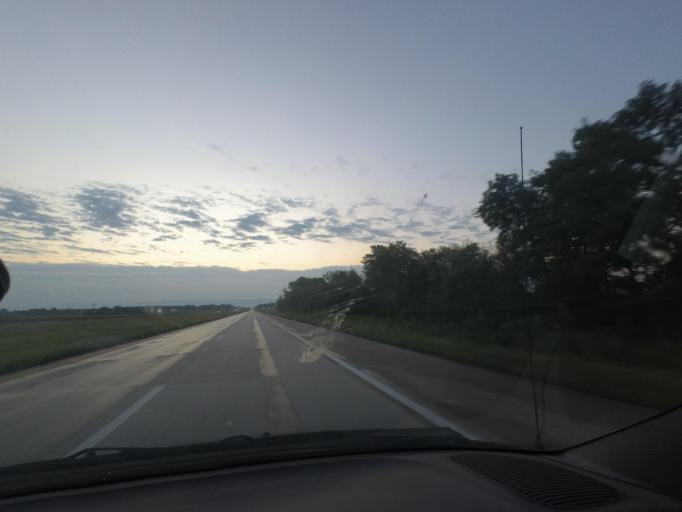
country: US
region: Missouri
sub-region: Macon County
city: Macon
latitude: 39.7598
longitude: -92.6825
